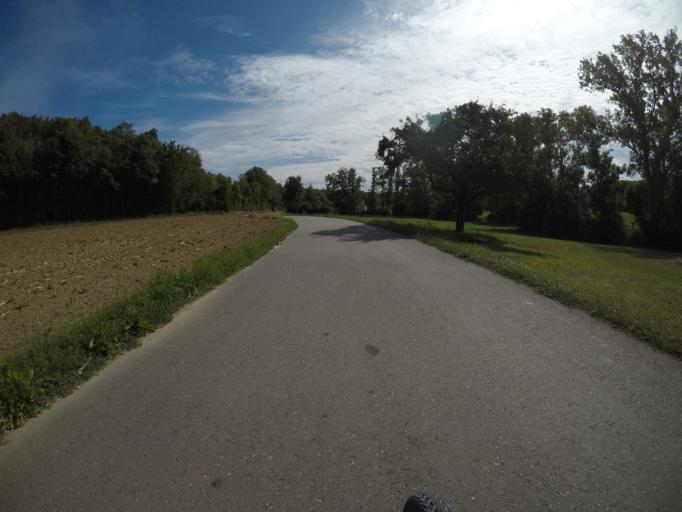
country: DE
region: Baden-Wuerttemberg
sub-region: Karlsruhe Region
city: Oberderdingen
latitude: 49.0936
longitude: 8.7648
